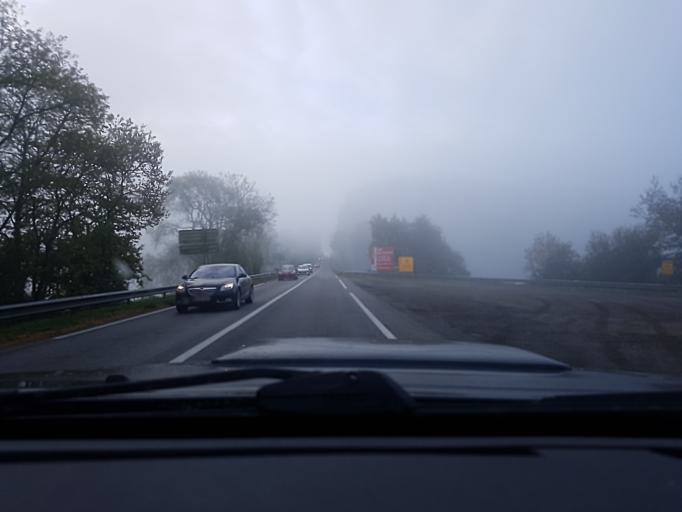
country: FR
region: Pays de la Loire
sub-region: Departement de la Vendee
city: Mache
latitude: 46.7704
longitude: -1.6667
